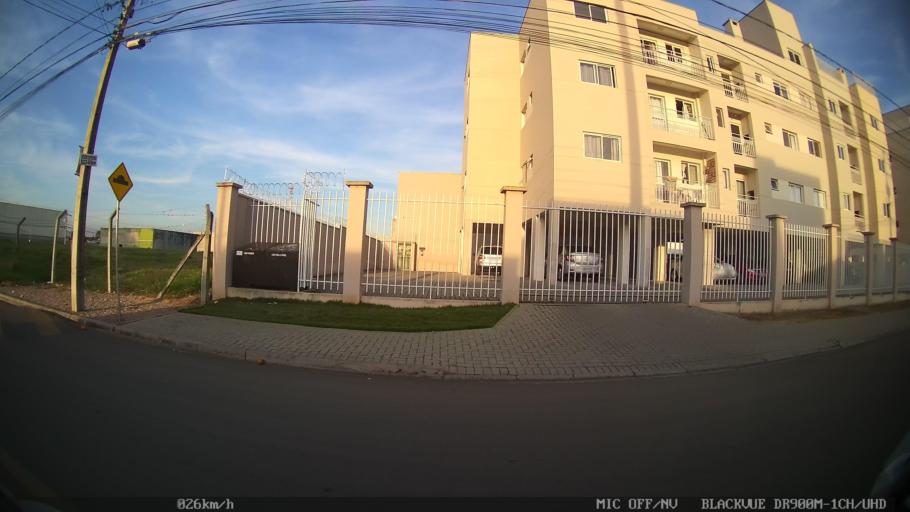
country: BR
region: Parana
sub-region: Pinhais
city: Pinhais
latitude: -25.4473
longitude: -49.1696
